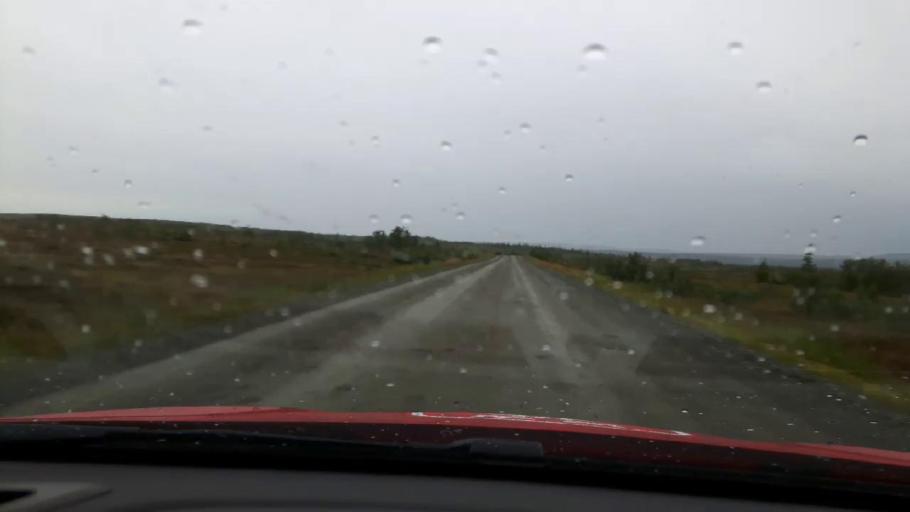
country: NO
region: Nord-Trondelag
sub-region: Meraker
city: Meraker
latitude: 63.6030
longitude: 12.2773
